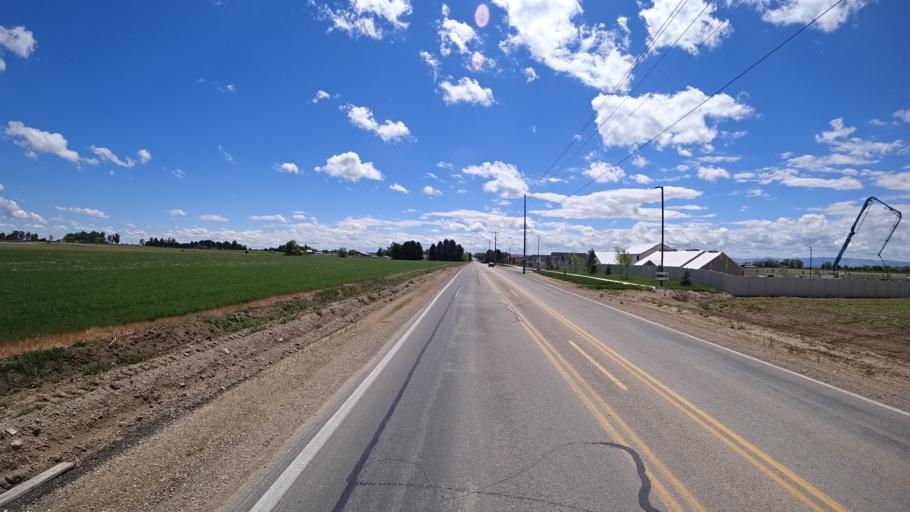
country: US
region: Idaho
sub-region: Ada County
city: Kuna
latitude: 43.5521
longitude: -116.4337
